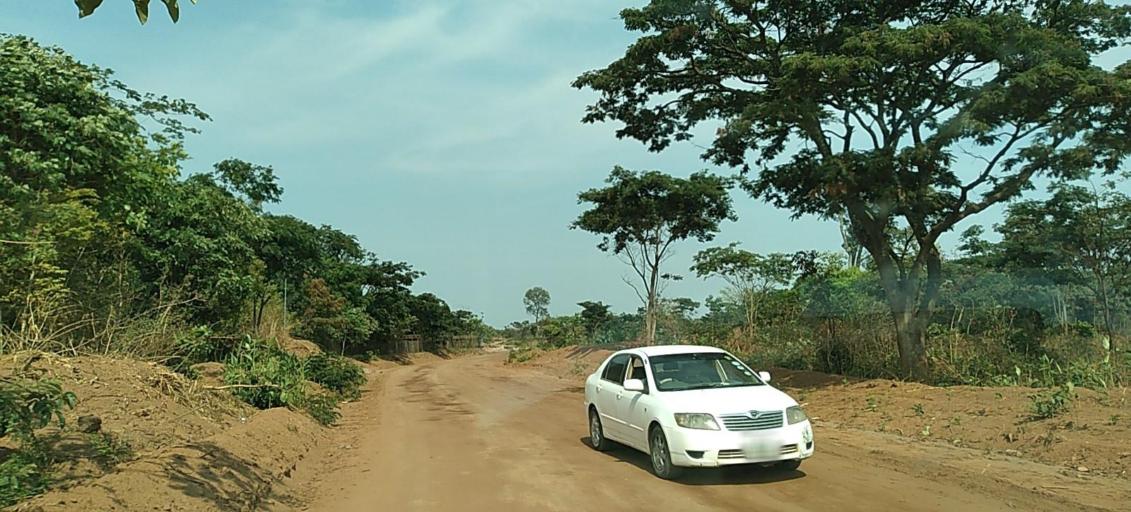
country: ZM
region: Copperbelt
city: Chililabombwe
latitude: -12.2922
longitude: 27.7662
